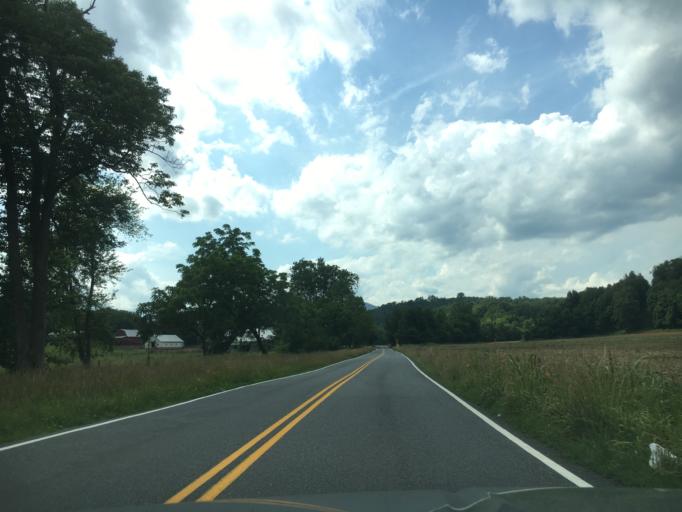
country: US
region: Virginia
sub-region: Roanoke County
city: Narrows
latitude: 37.1347
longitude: -79.9740
